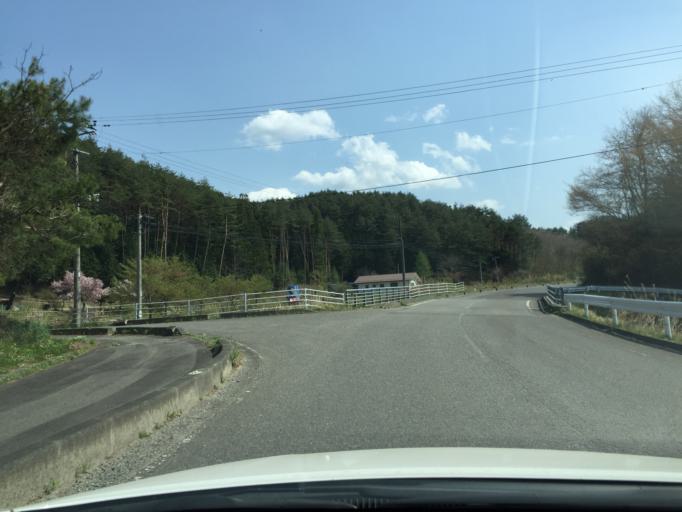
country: JP
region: Fukushima
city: Namie
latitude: 37.4131
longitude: 140.7961
